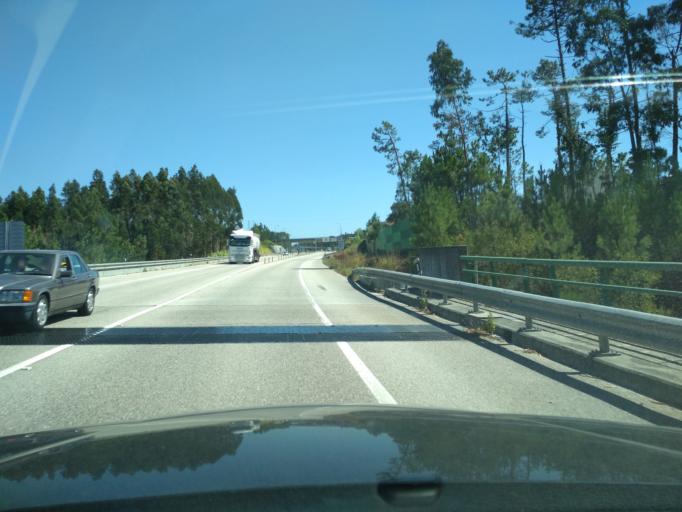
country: PT
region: Leiria
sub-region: Pombal
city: Lourical
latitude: 39.9873
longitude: -8.7355
